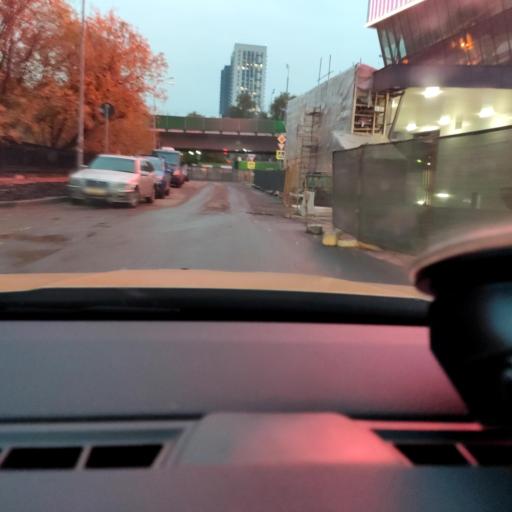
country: RU
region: Moscow
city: Gol'yanovo
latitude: 55.8113
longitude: 37.8030
